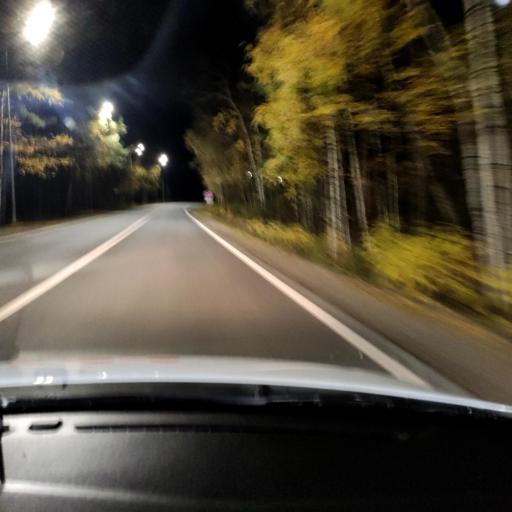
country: RU
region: Tatarstan
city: Verkhniy Uslon
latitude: 55.6381
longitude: 49.0225
